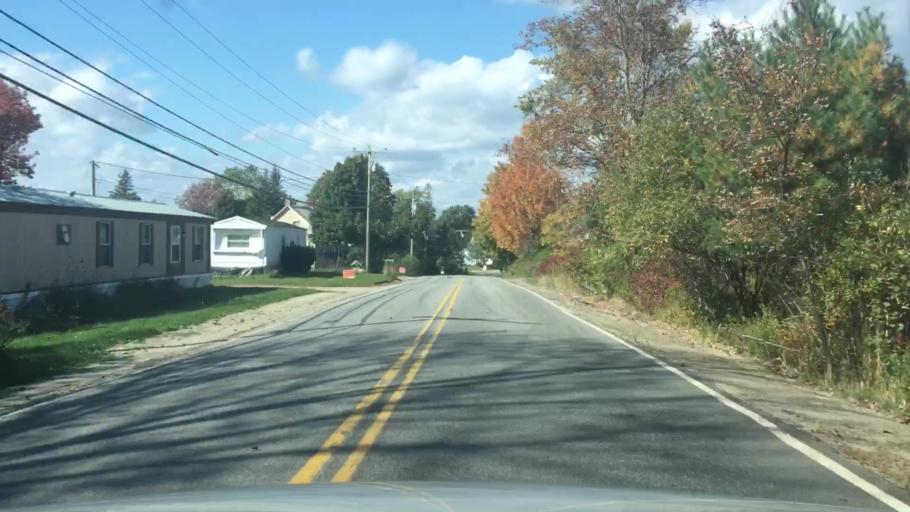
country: US
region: Maine
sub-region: Knox County
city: Warren
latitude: 44.1197
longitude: -69.2336
